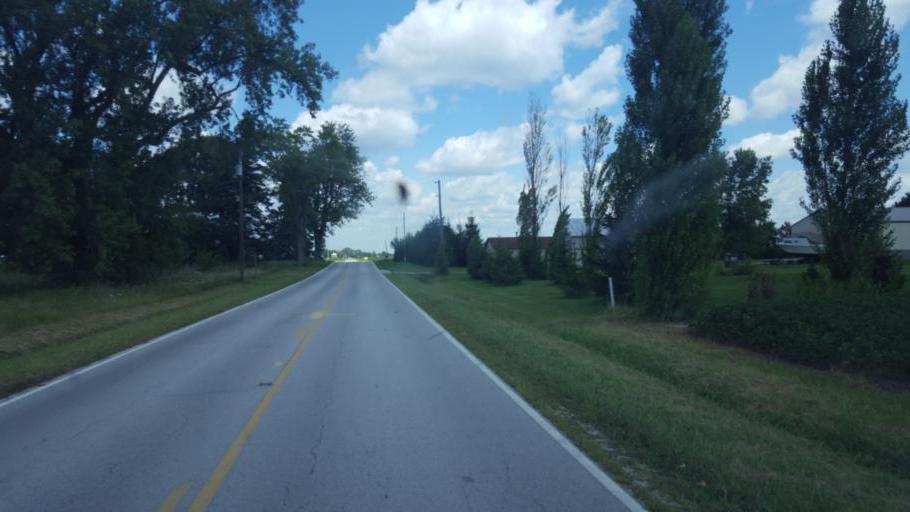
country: US
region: Ohio
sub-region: Sandusky County
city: Gibsonburg
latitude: 41.2762
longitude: -83.3116
